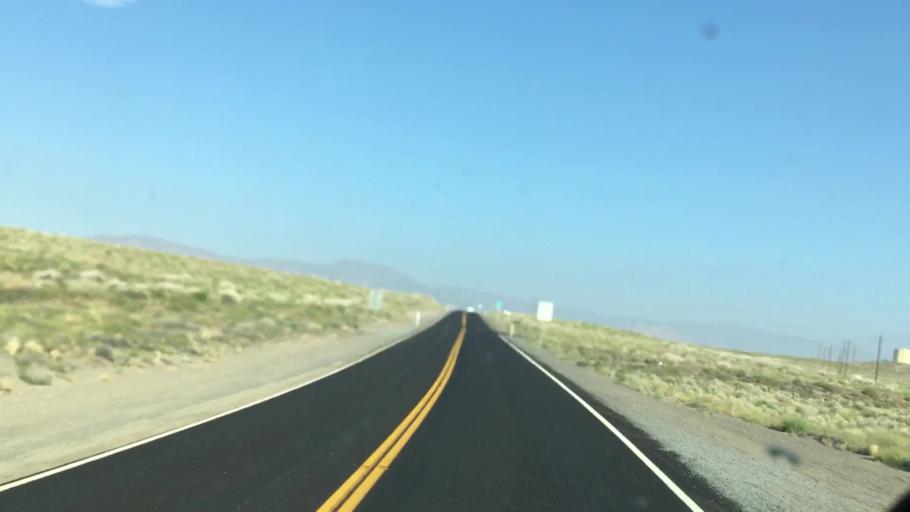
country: US
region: Nevada
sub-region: Lyon County
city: Fernley
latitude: 39.6388
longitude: -119.2931
